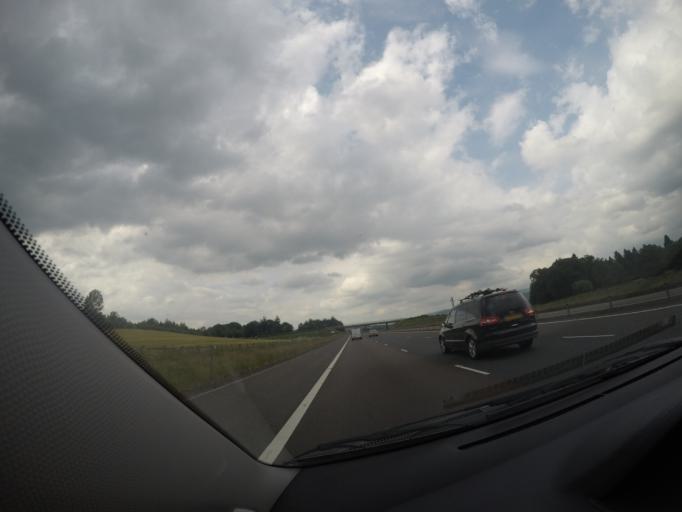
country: GB
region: Scotland
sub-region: Dumfries and Galloway
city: Moffat
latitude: 55.2988
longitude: -3.4429
